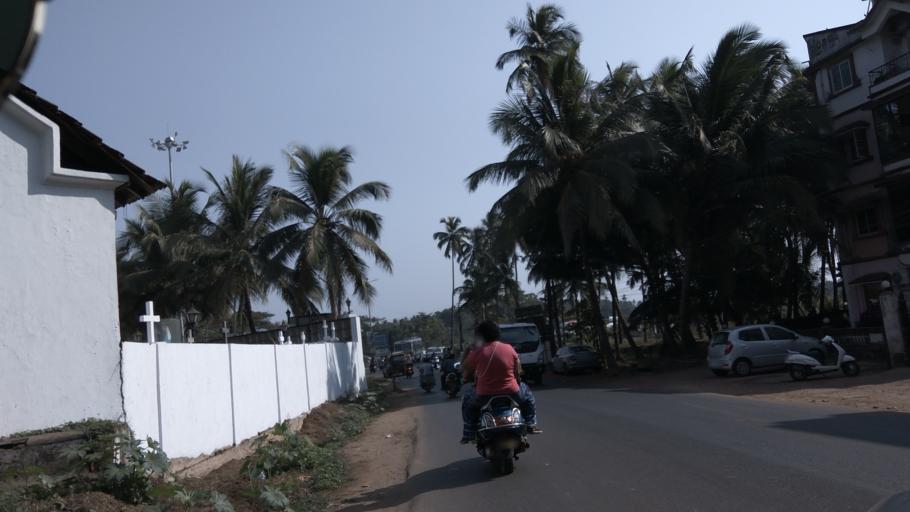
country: IN
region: Goa
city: Calangute
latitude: 15.5409
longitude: 73.7685
